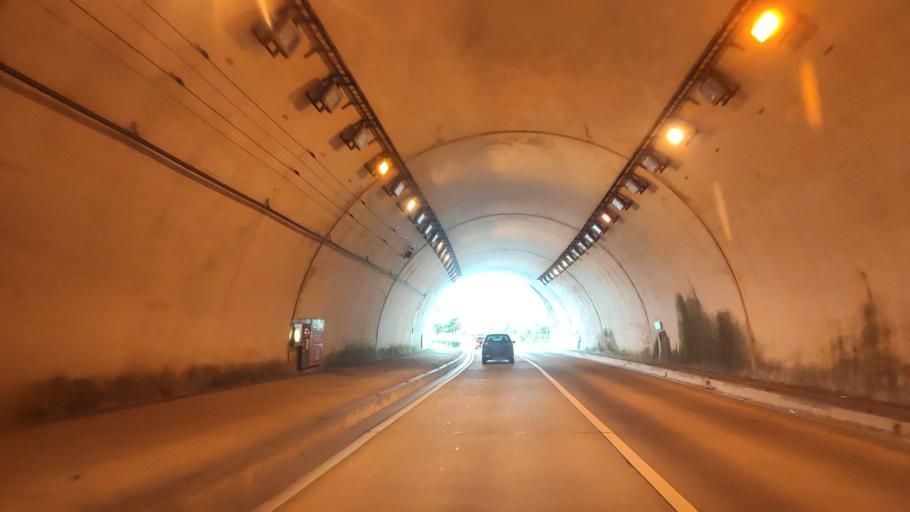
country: JP
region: Ehime
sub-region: Shikoku-chuo Shi
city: Matsuyama
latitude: 33.8872
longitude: 132.7070
